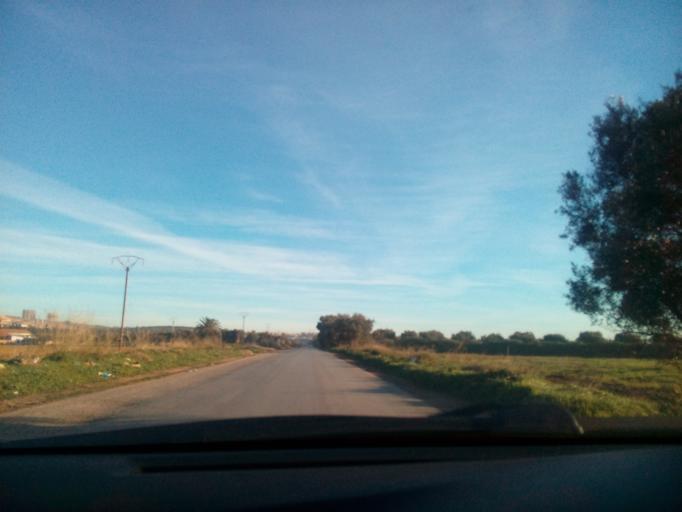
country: DZ
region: Oran
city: Es Senia
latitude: 35.6104
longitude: -0.6895
